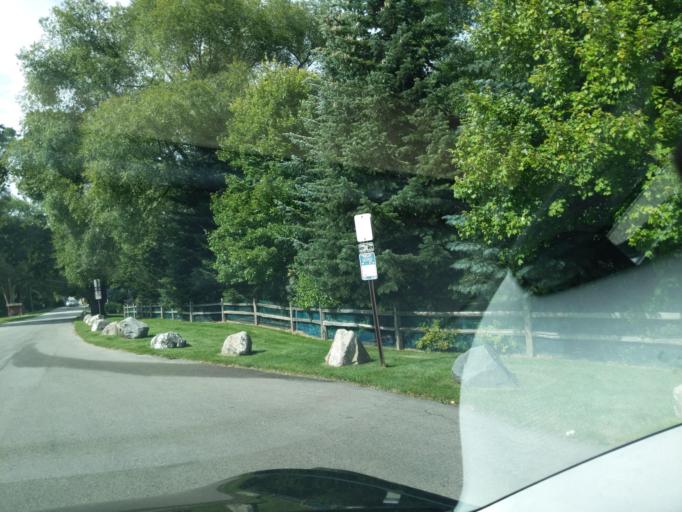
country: US
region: Michigan
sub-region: Antrim County
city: Bellaire
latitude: 45.0746
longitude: -85.3549
